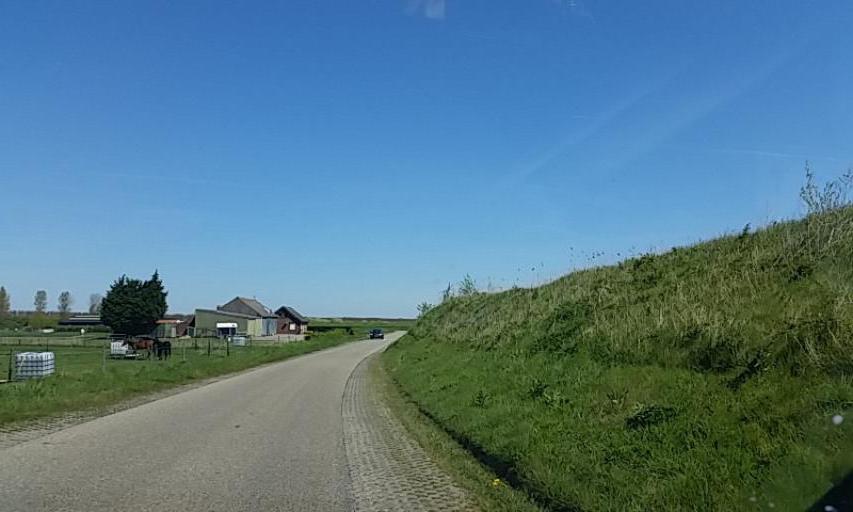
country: BE
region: Flanders
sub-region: Provincie Oost-Vlaanderen
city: Assenede
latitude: 51.3224
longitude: 3.7177
